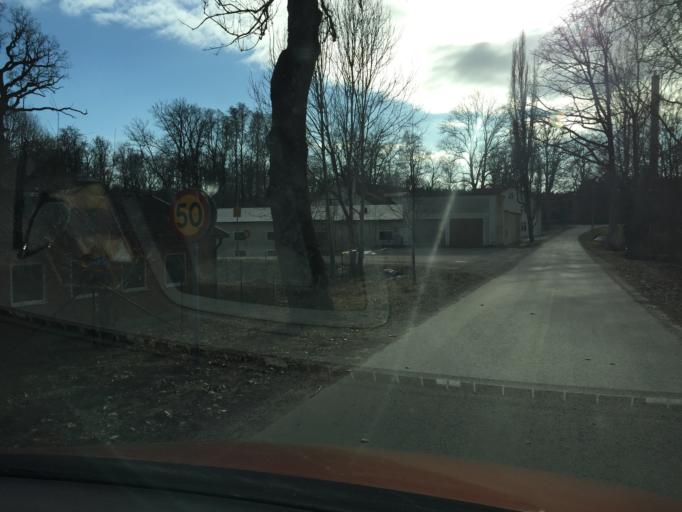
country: SE
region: Soedermanland
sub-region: Vingakers Kommun
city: Vingaker
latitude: 59.0259
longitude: 15.6770
